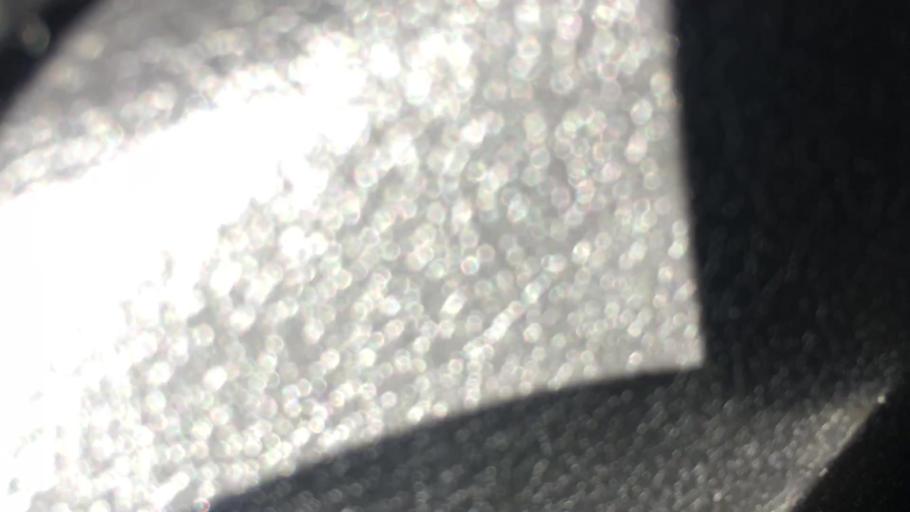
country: US
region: South Carolina
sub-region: Lexington County
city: Cayce
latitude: 33.9608
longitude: -81.0879
